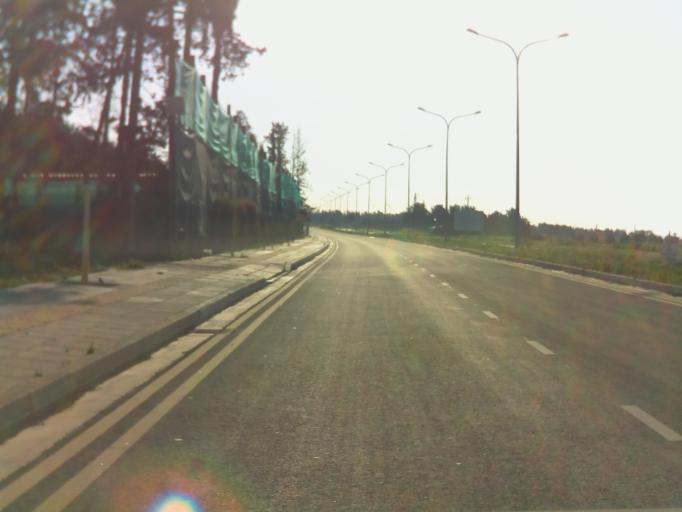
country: CY
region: Pafos
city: Paphos
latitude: 34.7425
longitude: 32.4470
